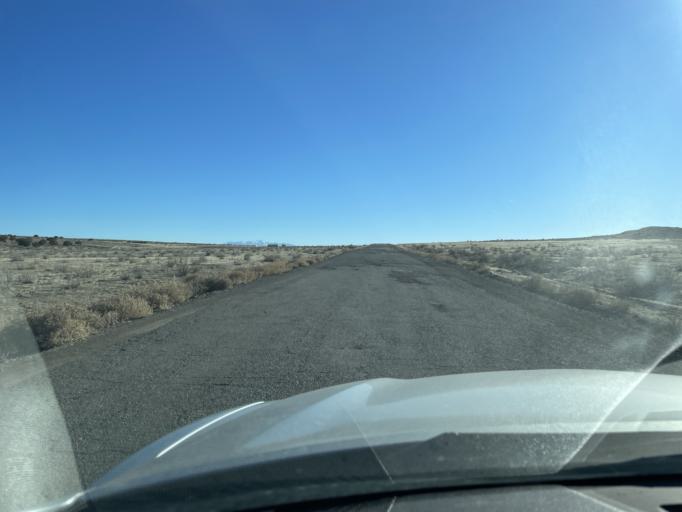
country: US
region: Colorado
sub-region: Mesa County
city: Loma
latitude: 39.1831
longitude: -109.1290
